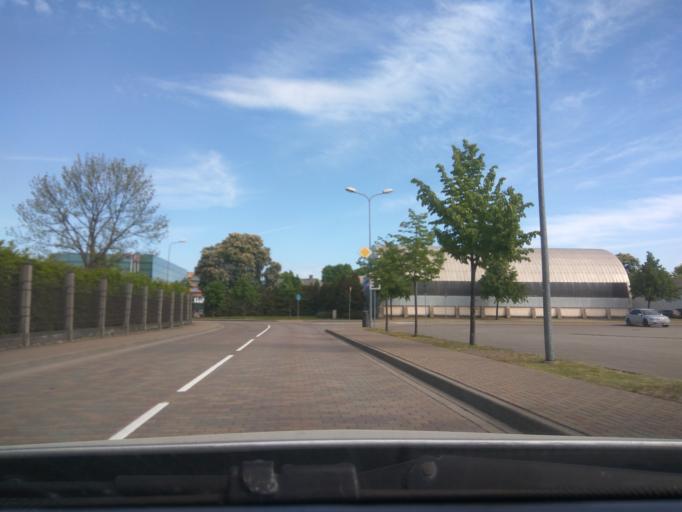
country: LV
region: Ventspils
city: Ventspils
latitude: 57.3973
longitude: 21.5707
